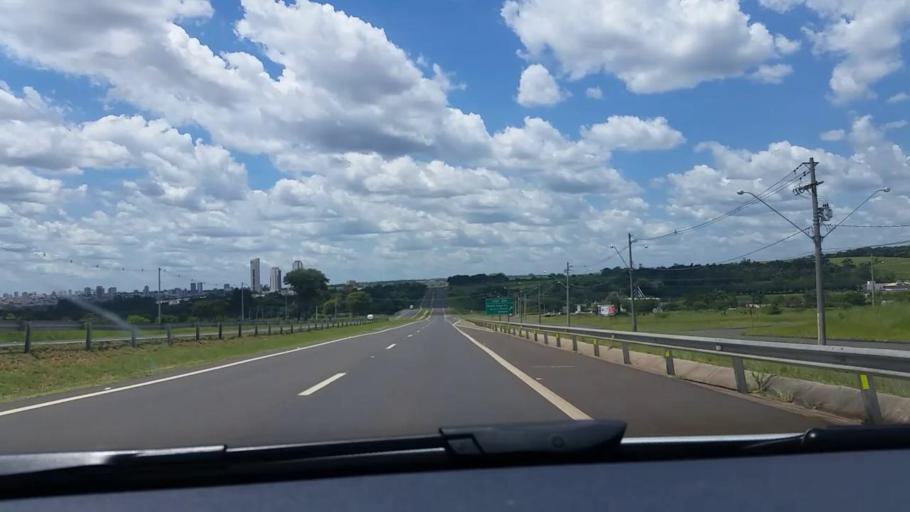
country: BR
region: Sao Paulo
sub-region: Bauru
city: Bauru
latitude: -22.3892
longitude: -49.0759
